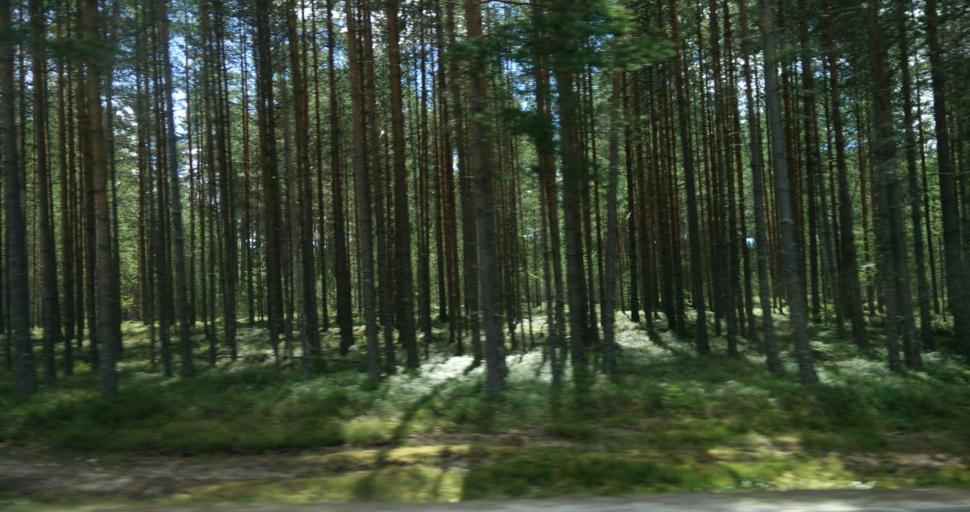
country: SE
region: Vaermland
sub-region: Hagfors Kommun
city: Ekshaerad
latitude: 60.0437
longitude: 13.5216
